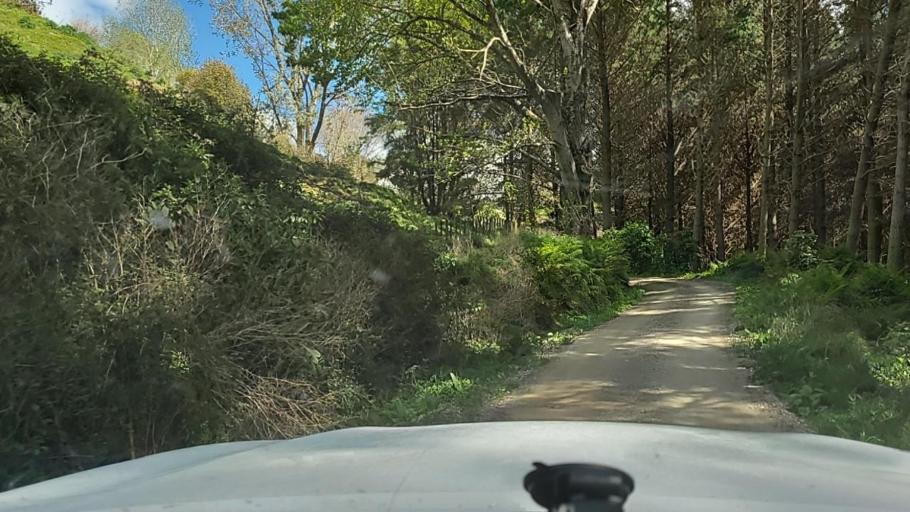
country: NZ
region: Gisborne
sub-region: Gisborne District
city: Gisborne
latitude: -38.7853
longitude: 177.7746
